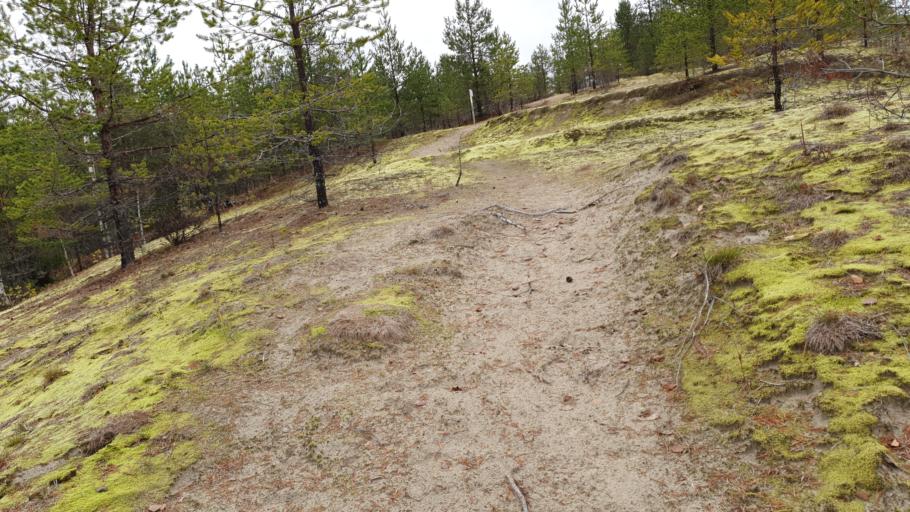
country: FI
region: Kainuu
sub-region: Kehys-Kainuu
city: Kuhmo
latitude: 64.1521
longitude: 29.3935
